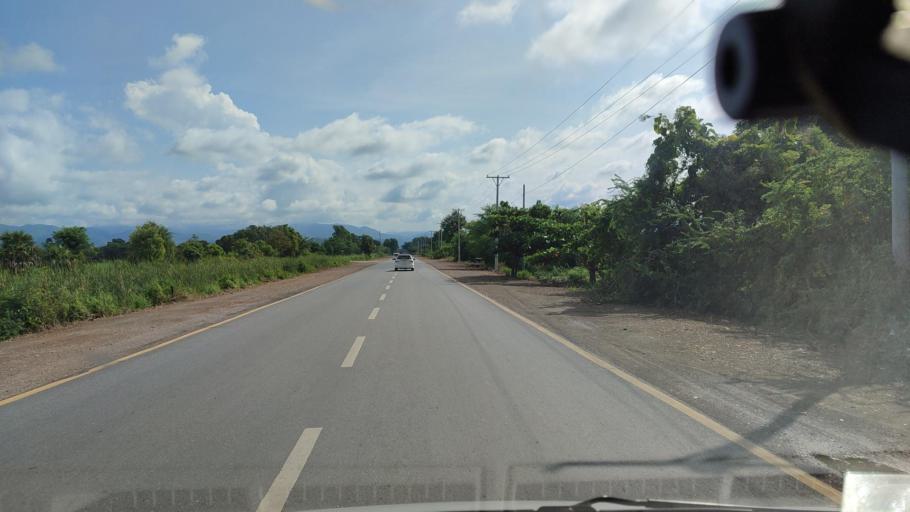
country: MM
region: Mandalay
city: Mandalay
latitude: 21.8676
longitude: 96.1661
